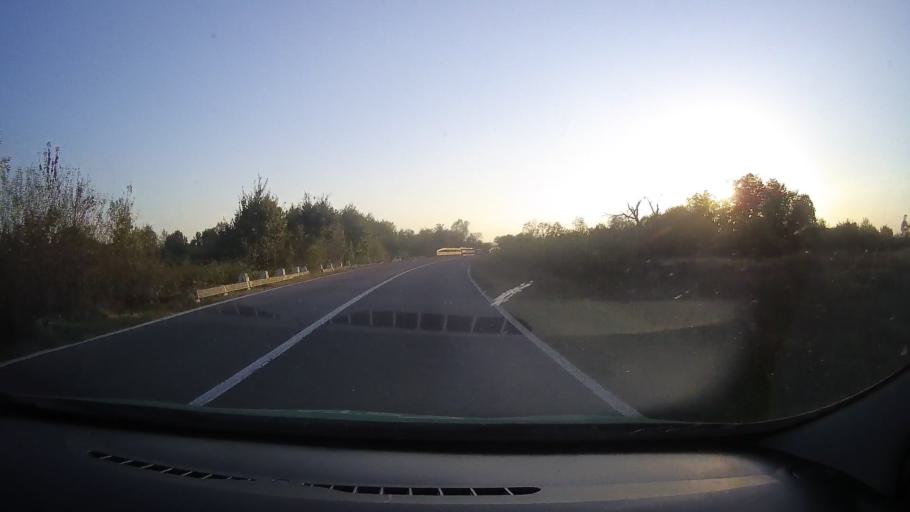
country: RO
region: Timis
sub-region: Comuna Traian Vuia
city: Traian Vuia
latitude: 45.7875
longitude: 22.0601
